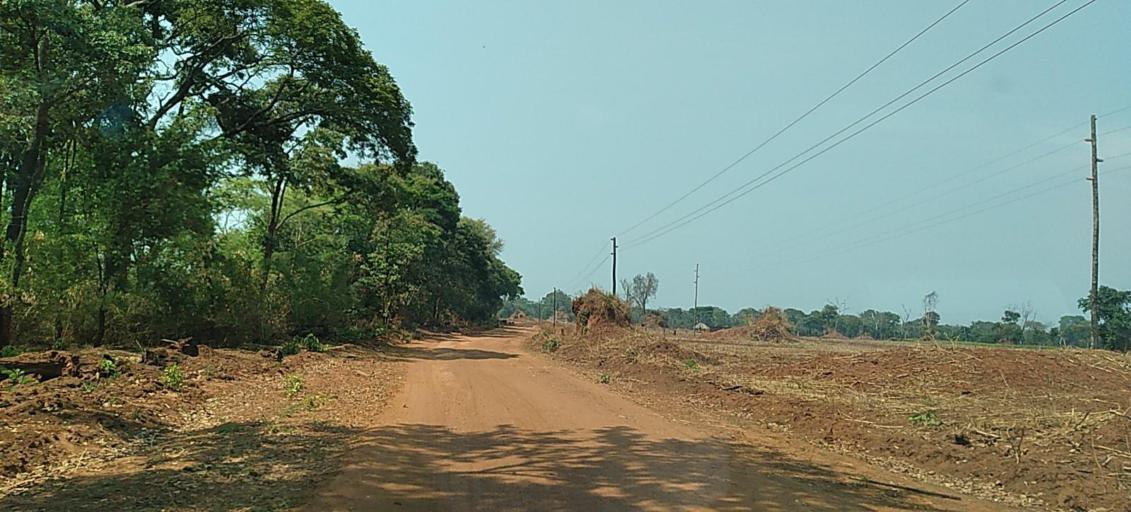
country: ZM
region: Copperbelt
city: Chingola
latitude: -13.0656
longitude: 27.4170
